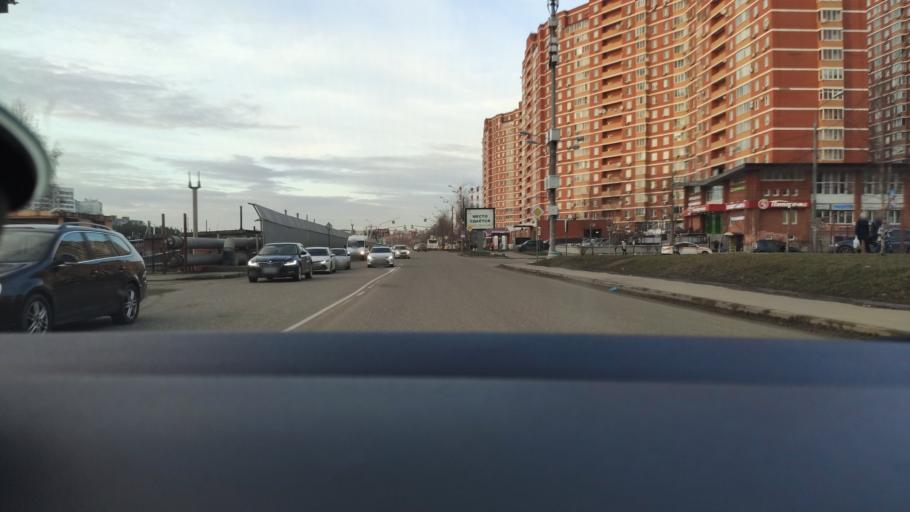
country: RU
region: Moskovskaya
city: Vidnoye
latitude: 55.5415
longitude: 37.7200
